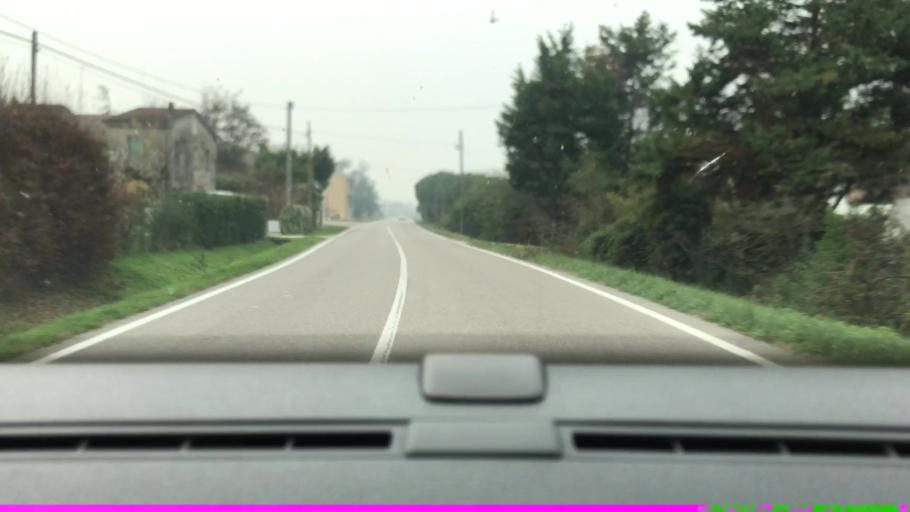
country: IT
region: Lombardy
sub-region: Provincia di Mantova
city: San Giacomo delle Segnate
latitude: 44.9701
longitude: 11.0216
